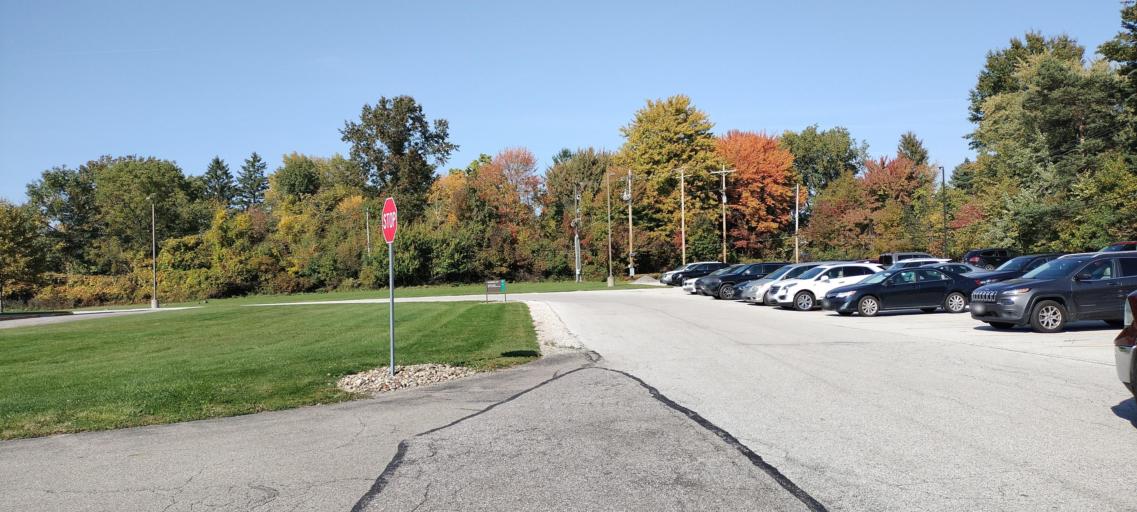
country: US
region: Ohio
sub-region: Cuyahoga County
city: Mayfield Heights
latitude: 41.5368
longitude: -81.4581
